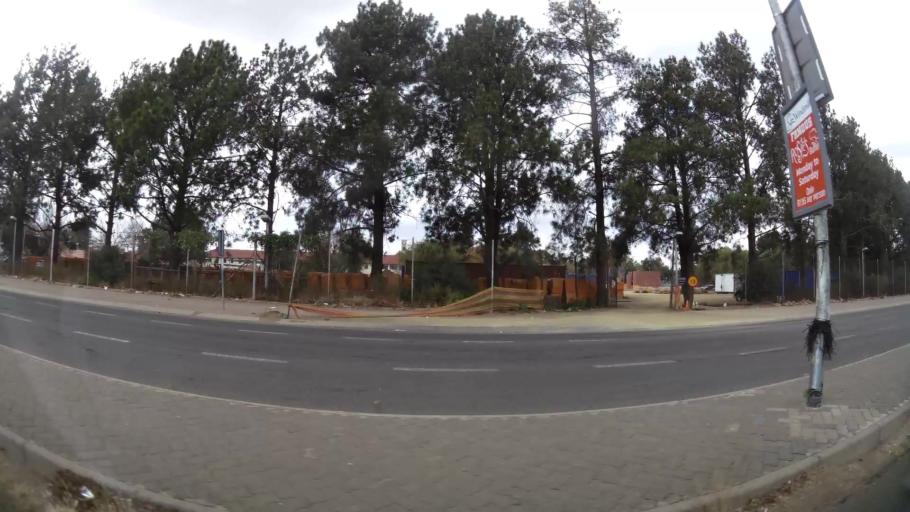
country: ZA
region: Orange Free State
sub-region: Mangaung Metropolitan Municipality
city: Bloemfontein
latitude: -29.1199
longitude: 26.2104
